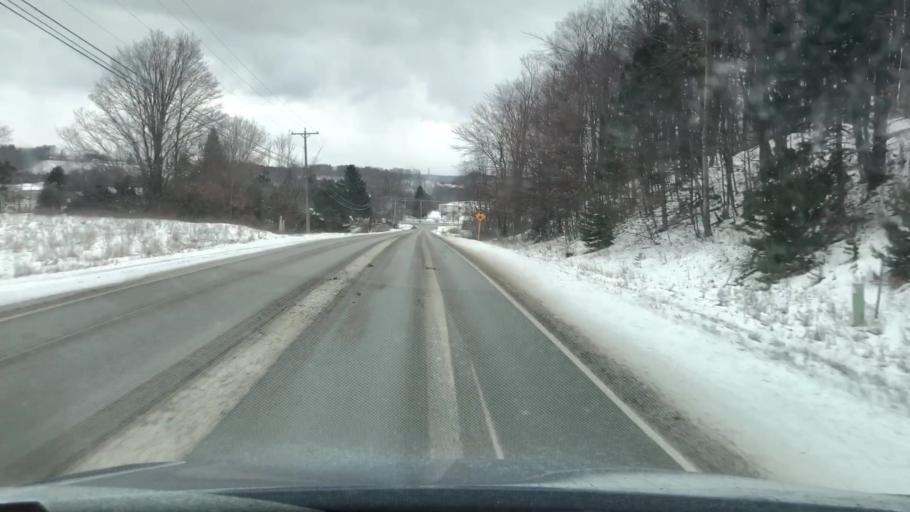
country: US
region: Michigan
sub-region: Grand Traverse County
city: Traverse City
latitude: 44.7154
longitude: -85.6311
